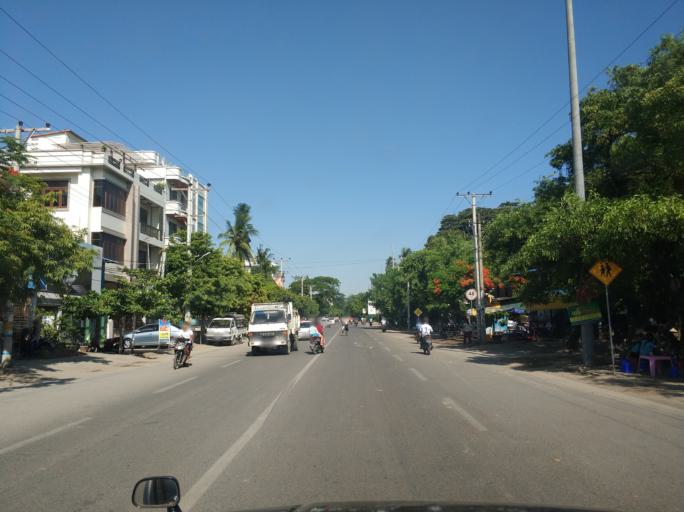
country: MM
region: Mandalay
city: Mandalay
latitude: 21.9705
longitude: 96.0662
